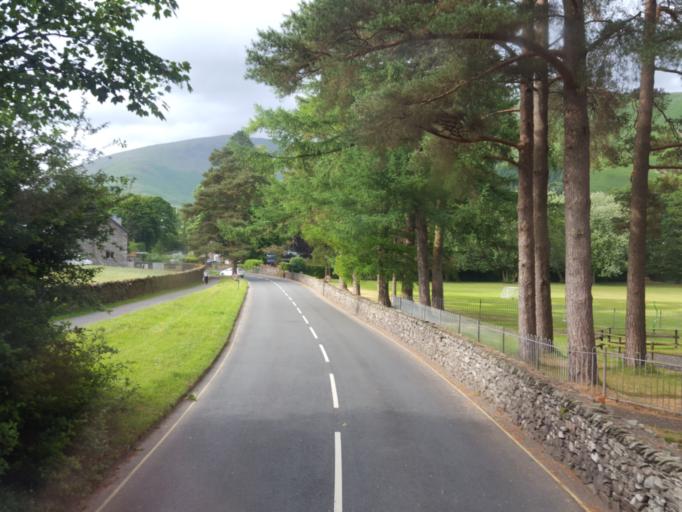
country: GB
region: England
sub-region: Cumbria
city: Ambleside
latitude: 54.4613
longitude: -3.0227
